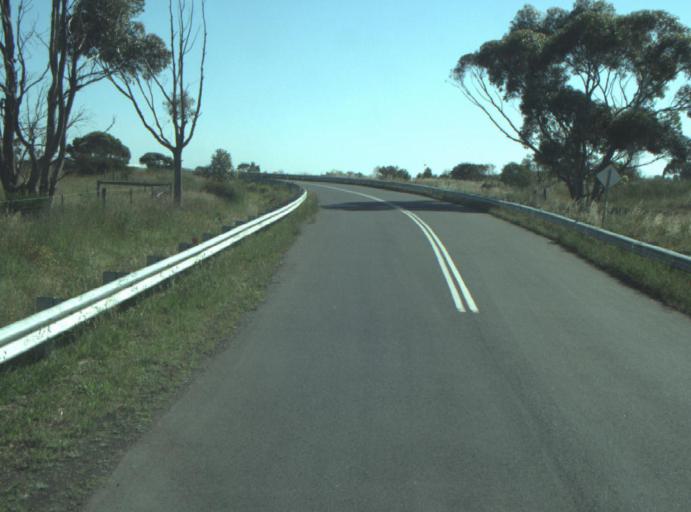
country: AU
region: Victoria
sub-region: Wyndham
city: Little River
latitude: -37.9890
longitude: 144.4575
